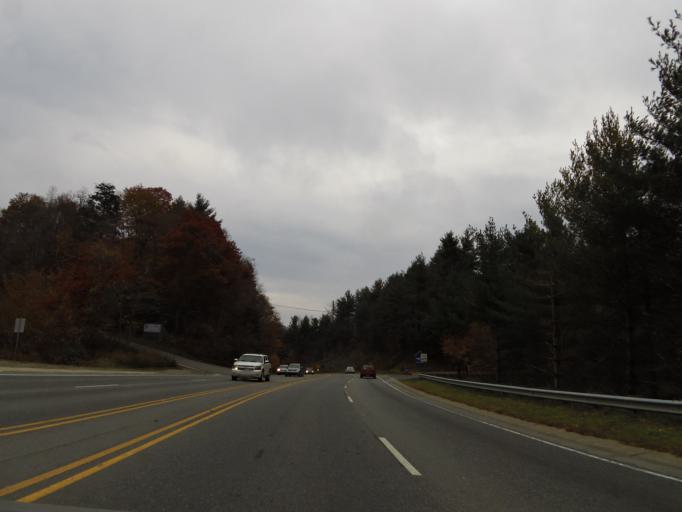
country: US
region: North Carolina
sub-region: Watauga County
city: Boone
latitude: 36.1840
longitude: -81.6508
